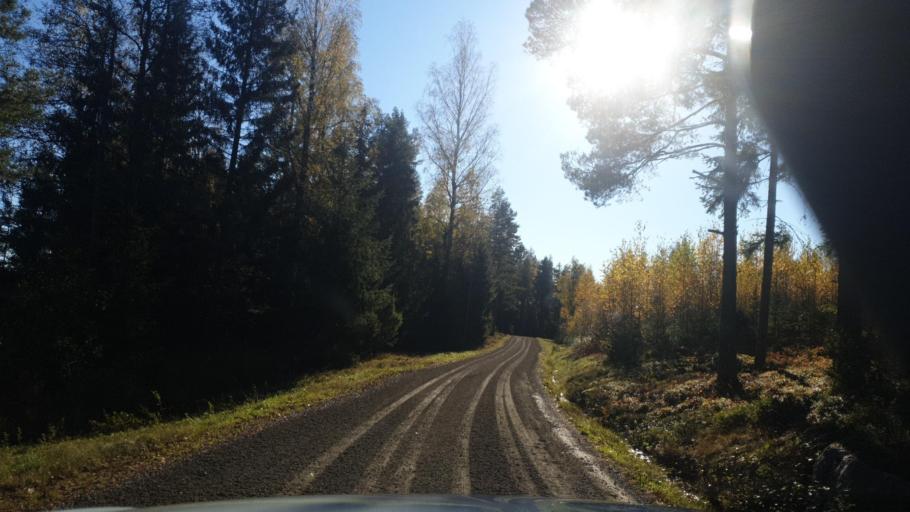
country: SE
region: Vaermland
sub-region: Grums Kommun
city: Grums
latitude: 59.5061
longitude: 12.9270
